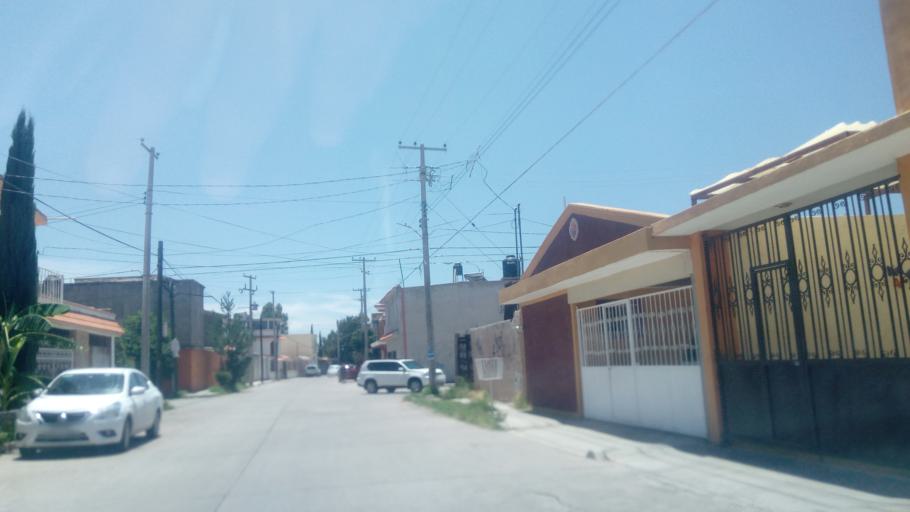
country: MX
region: Durango
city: Victoria de Durango
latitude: 23.9971
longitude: -104.6474
